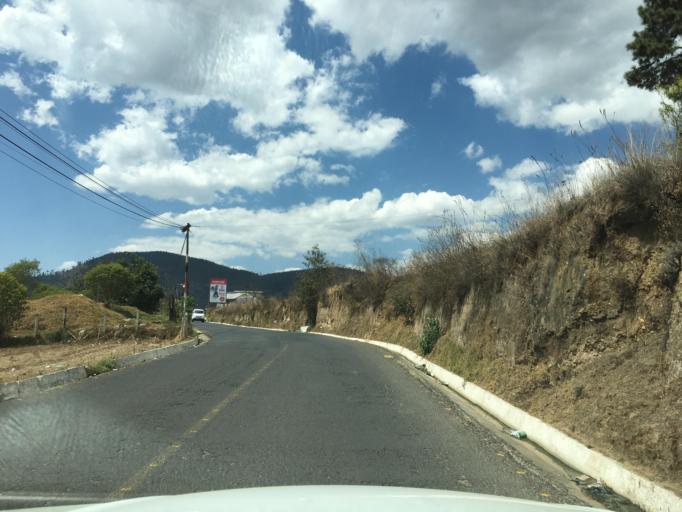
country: GT
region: Totonicapan
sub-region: Municipio de San Andres Xecul
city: San Andres Xecul
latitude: 14.9051
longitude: -91.4638
